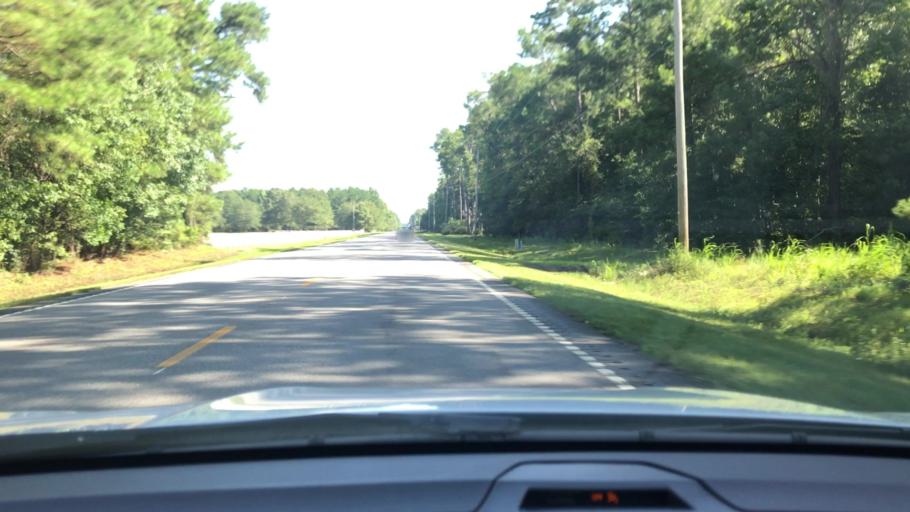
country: US
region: South Carolina
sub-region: Horry County
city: Conway
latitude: 33.7424
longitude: -79.0800
